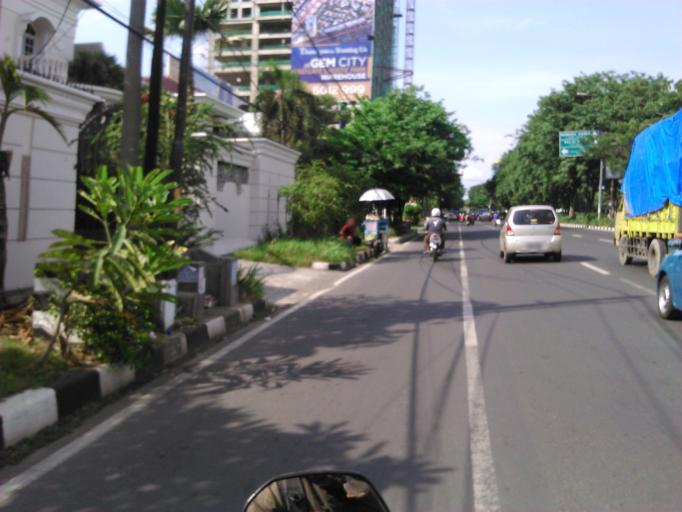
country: ID
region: East Java
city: Mulyorejo
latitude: -7.2784
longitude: 112.7812
